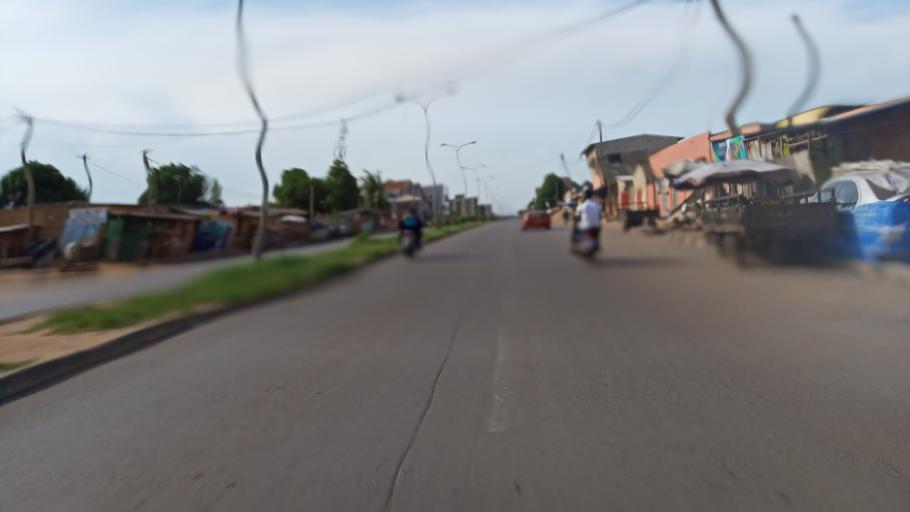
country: TG
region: Maritime
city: Lome
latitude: 6.1705
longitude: 1.2672
